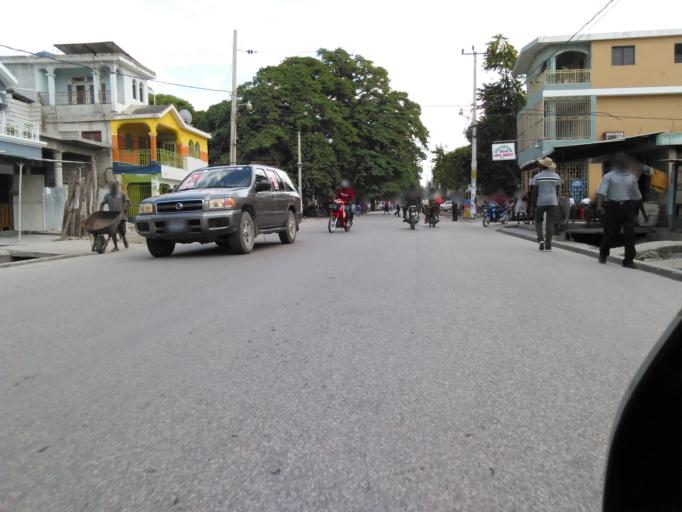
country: HT
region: Artibonite
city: Saint-Marc
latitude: 19.1068
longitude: -72.6968
